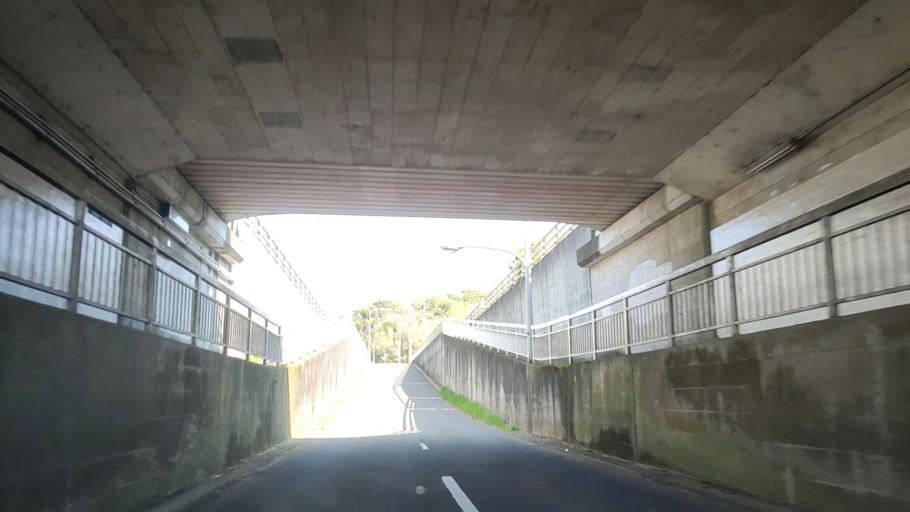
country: JP
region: Kanagawa
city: Oiso
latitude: 35.3077
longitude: 139.2968
